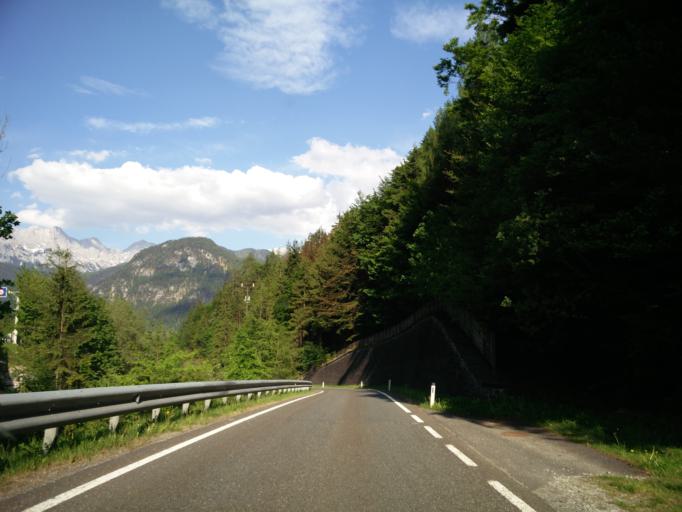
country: AT
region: Salzburg
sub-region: Politischer Bezirk Zell am See
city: Lofer
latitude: 47.5788
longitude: 12.6714
